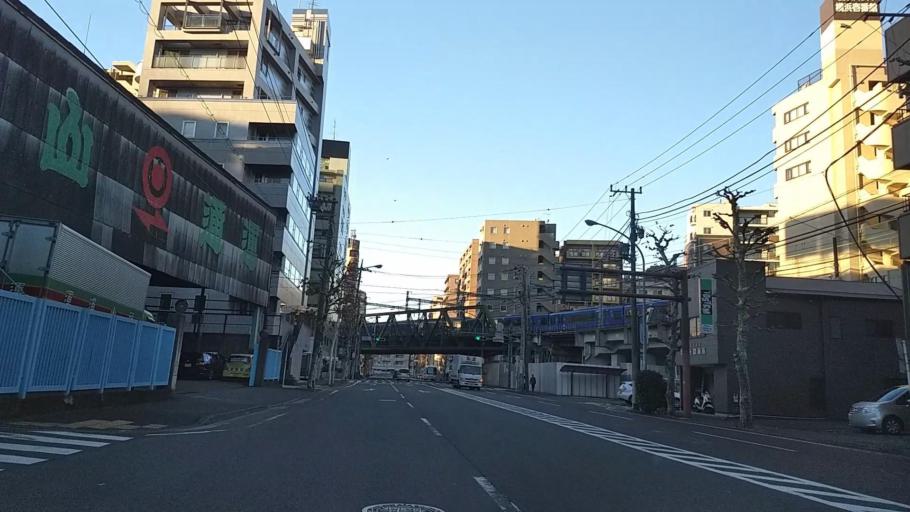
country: JP
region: Kanagawa
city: Yokohama
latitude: 35.4596
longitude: 139.6193
